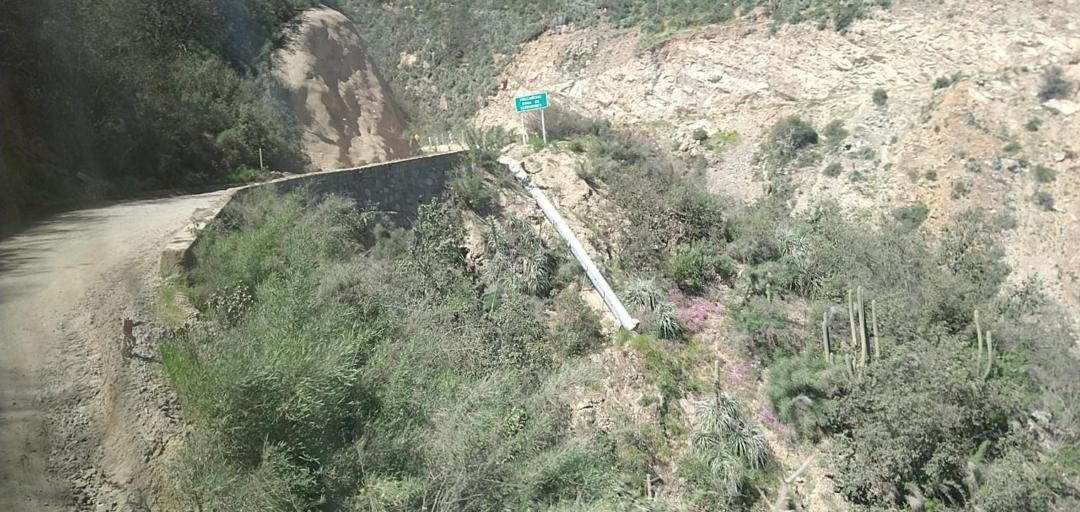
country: CL
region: Valparaiso
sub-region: Provincia de Marga Marga
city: Limache
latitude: -33.2008
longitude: -71.2610
